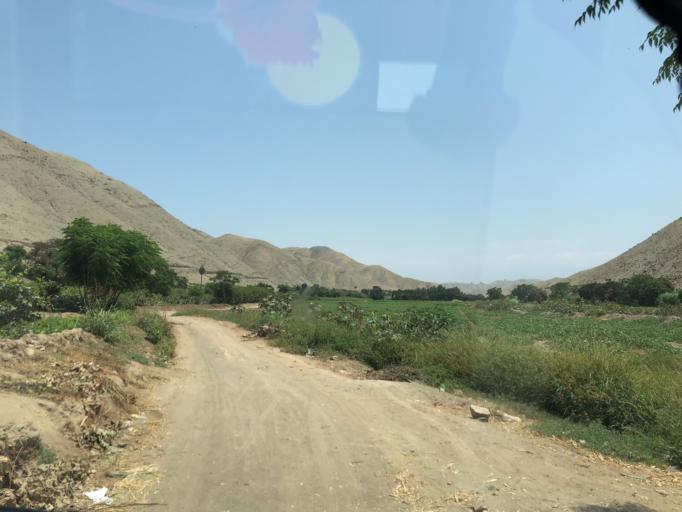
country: PE
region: Lima
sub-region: Provincia de Canete
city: Quilmana
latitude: -12.9890
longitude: -76.4358
